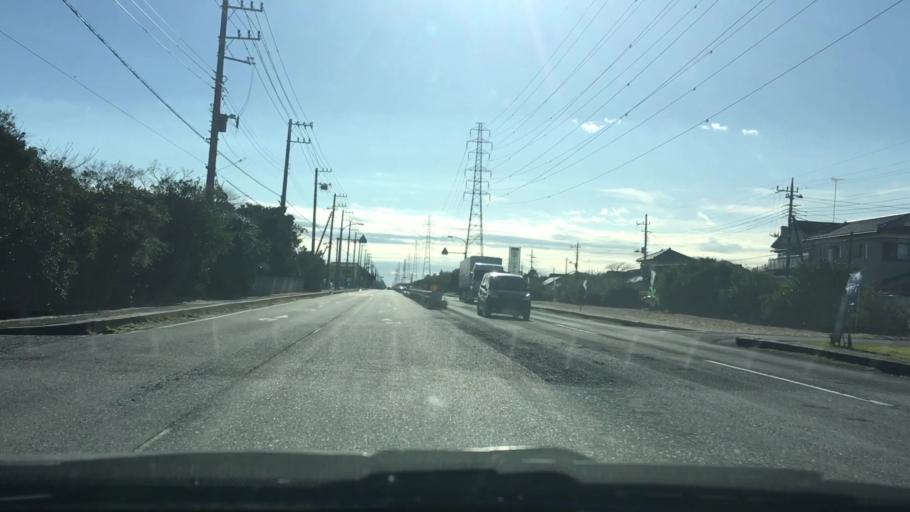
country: JP
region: Chiba
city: Omigawa
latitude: 35.8734
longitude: 140.7210
